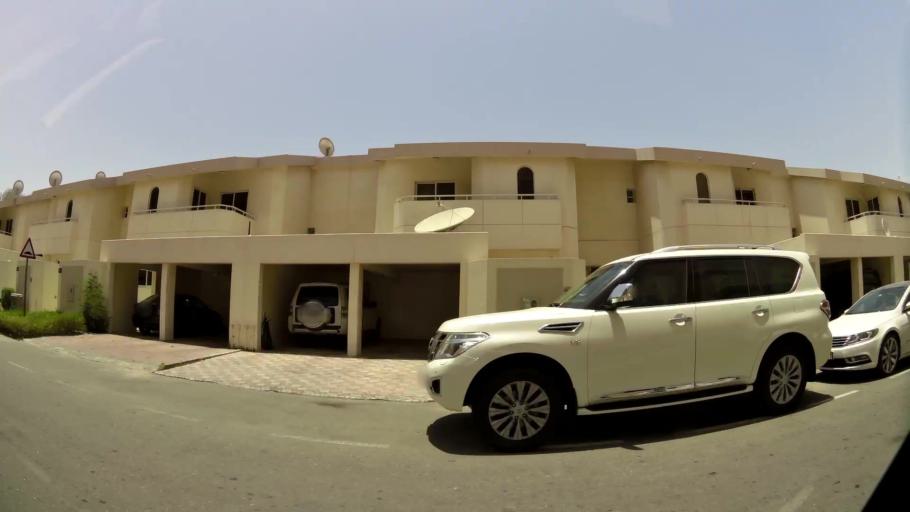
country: AE
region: Dubai
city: Dubai
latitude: 25.1794
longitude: 55.2470
